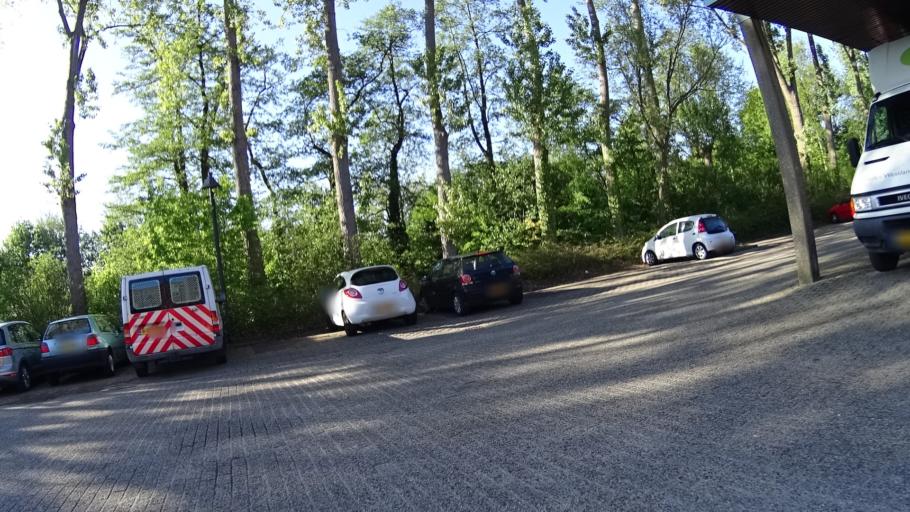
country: NL
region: South Holland
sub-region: Gemeente Delft
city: Delft
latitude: 52.0168
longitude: 4.3668
